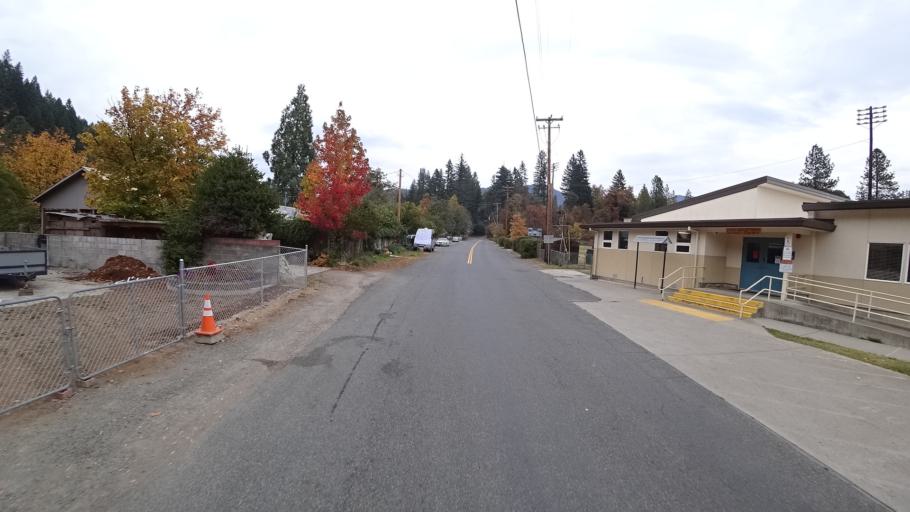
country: US
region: California
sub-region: Siskiyou County
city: Happy Camp
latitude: 41.7956
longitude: -123.3785
